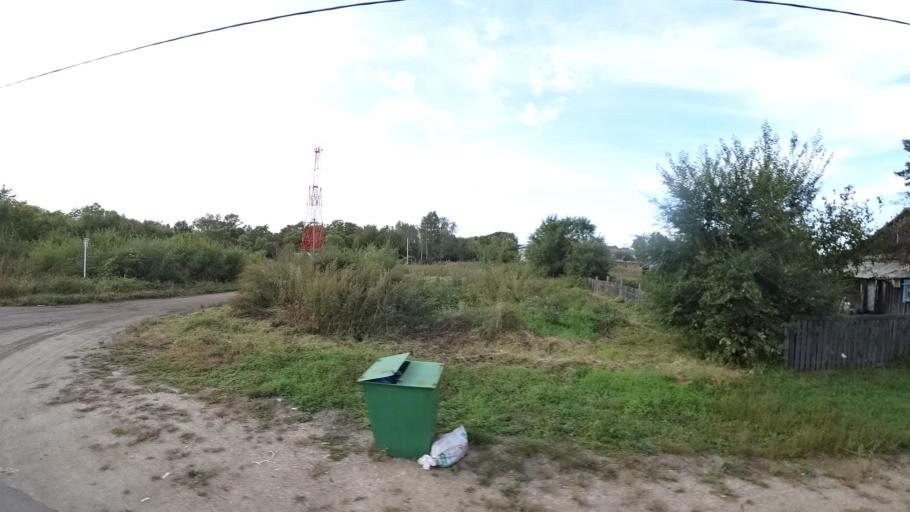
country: RU
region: Amur
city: Arkhara
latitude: 49.3612
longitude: 130.1201
